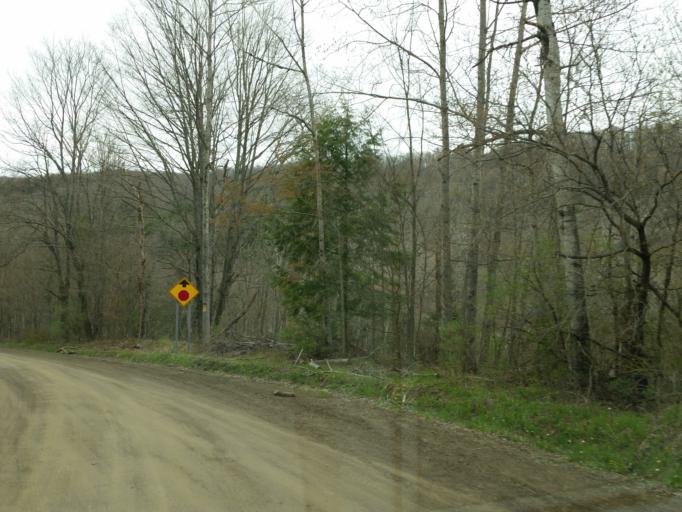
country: US
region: New York
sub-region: Allegany County
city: Andover
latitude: 42.0493
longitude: -77.7454
